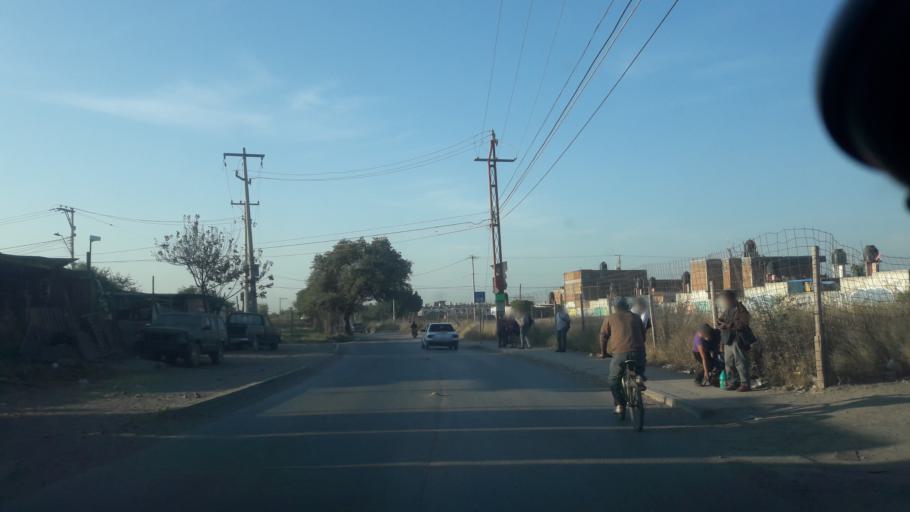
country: MX
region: Guanajuato
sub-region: Leon
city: Medina
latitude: 21.1698
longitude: -101.6400
